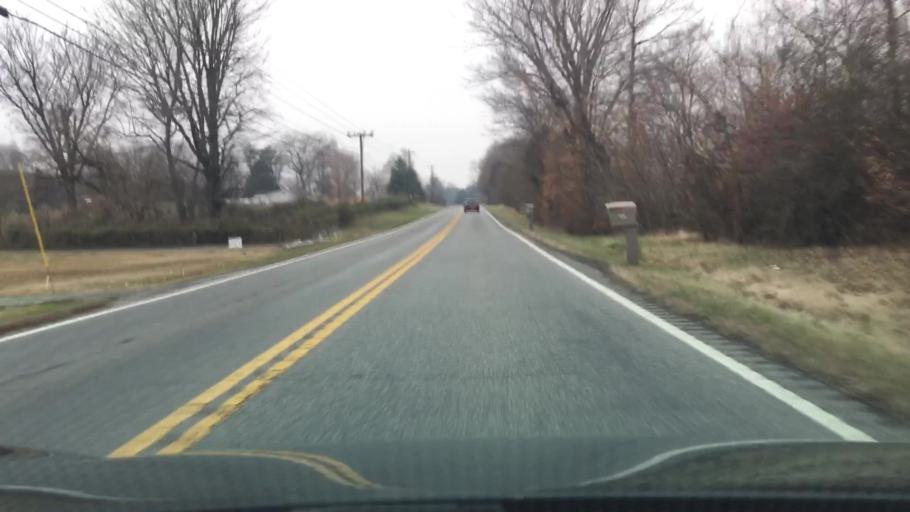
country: US
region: Kentucky
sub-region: Livingston County
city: Ledbetter
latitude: 36.9665
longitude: -88.4443
